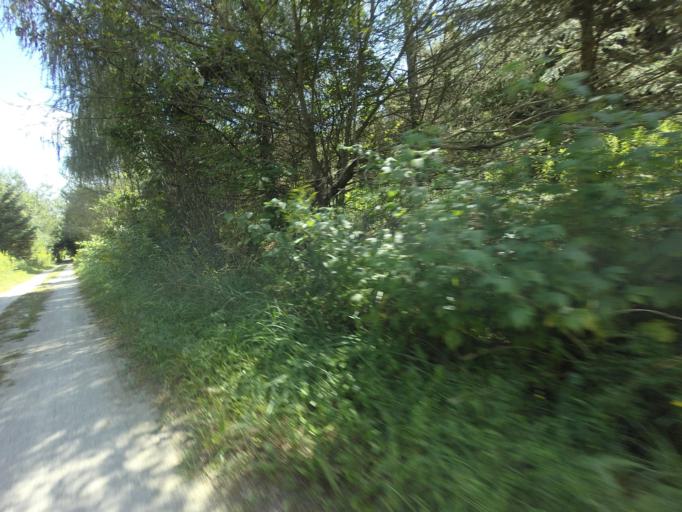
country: CA
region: Ontario
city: Orangeville
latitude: 43.7767
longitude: -80.1116
